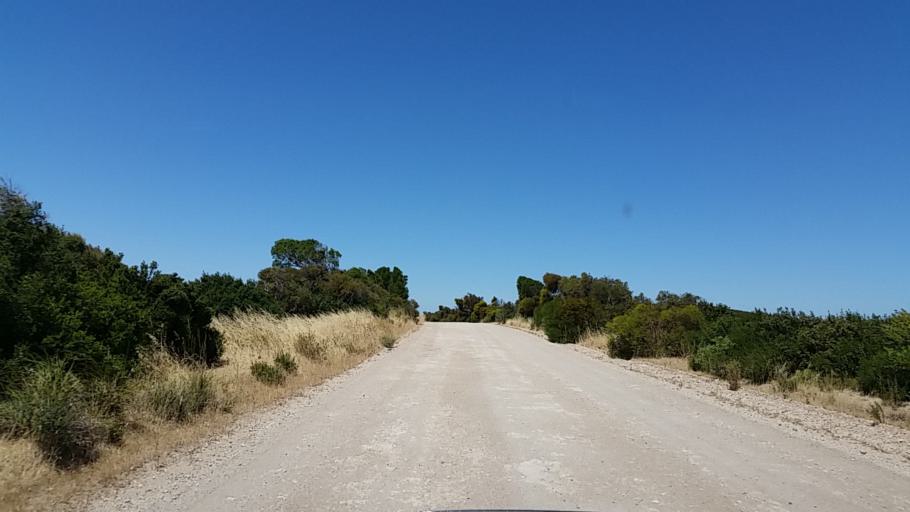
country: AU
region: South Australia
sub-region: Yorke Peninsula
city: Honiton
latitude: -35.0920
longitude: 137.4476
